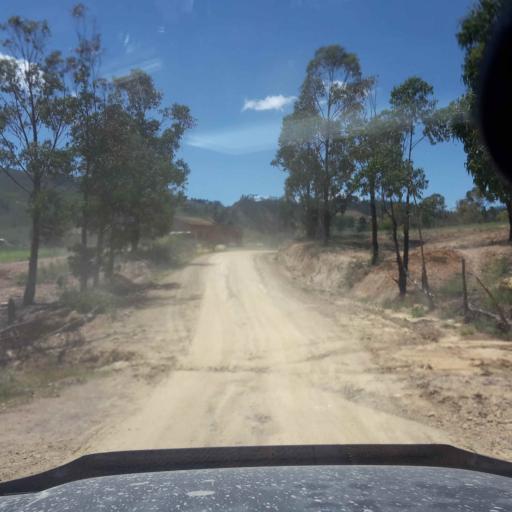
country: BO
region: Cochabamba
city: Totora
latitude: -17.7635
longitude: -65.2338
